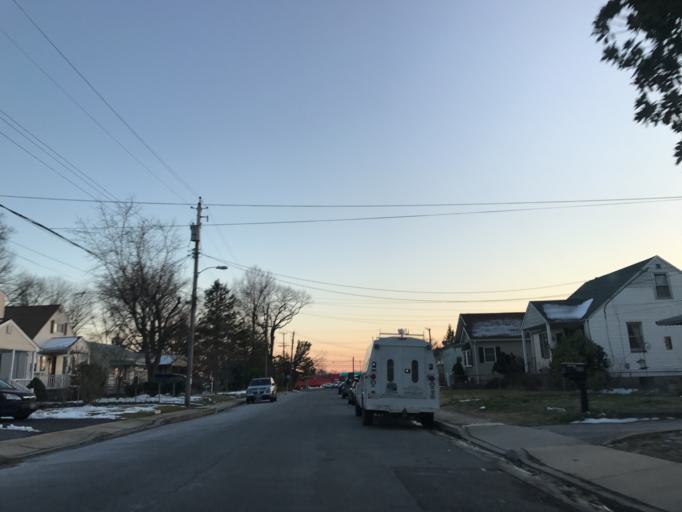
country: US
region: Maryland
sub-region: Baltimore County
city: Middle River
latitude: 39.3122
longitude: -76.4459
